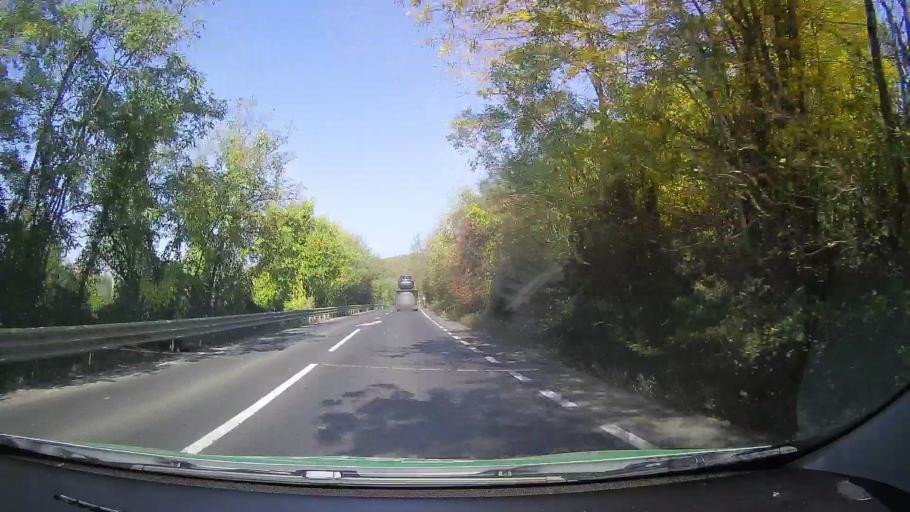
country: RO
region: Arad
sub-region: Comuna Bata
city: Bata
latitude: 46.0409
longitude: 22.0595
